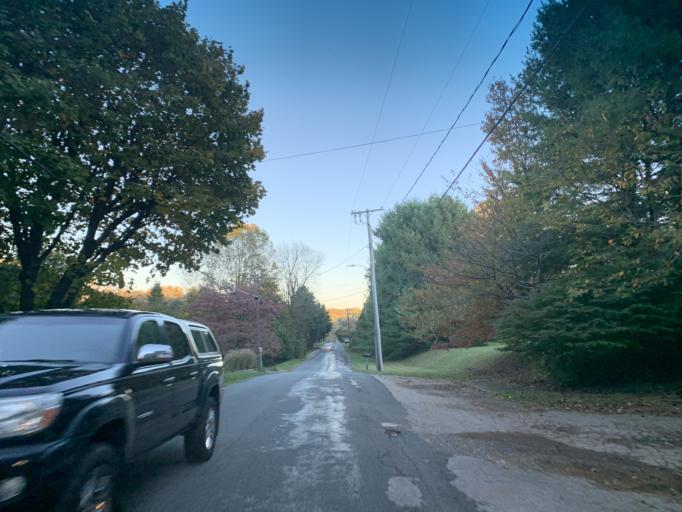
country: US
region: Maryland
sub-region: Baltimore County
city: Kingsville
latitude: 39.4689
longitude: -76.4166
